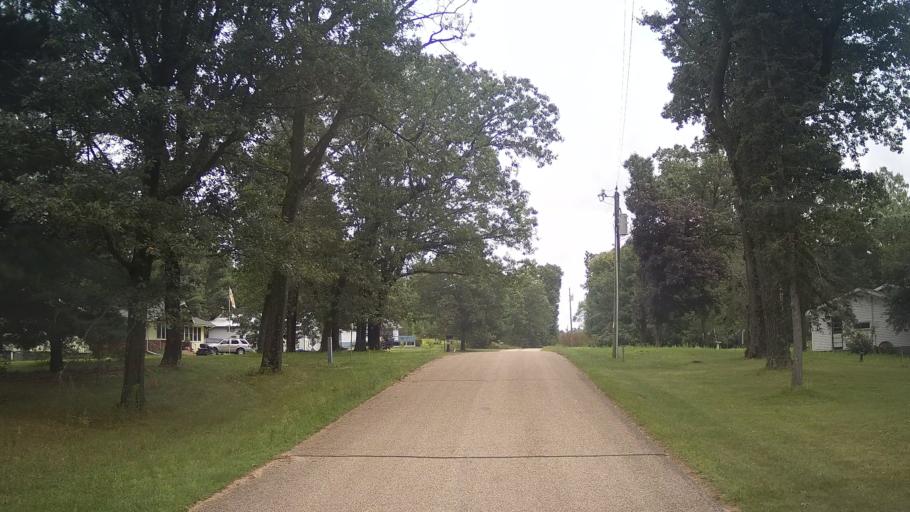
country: US
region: Wisconsin
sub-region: Adams County
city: Friendship
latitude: 44.0333
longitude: -89.8964
